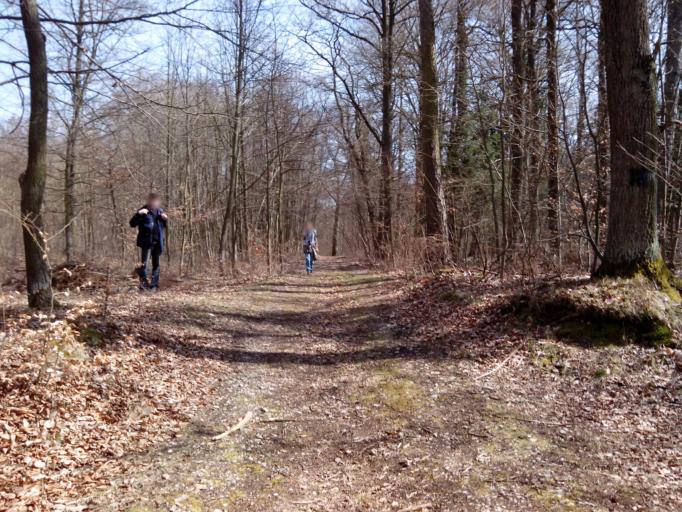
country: CZ
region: Central Bohemia
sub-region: Okres Beroun
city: Beroun
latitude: 49.9376
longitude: 14.1068
